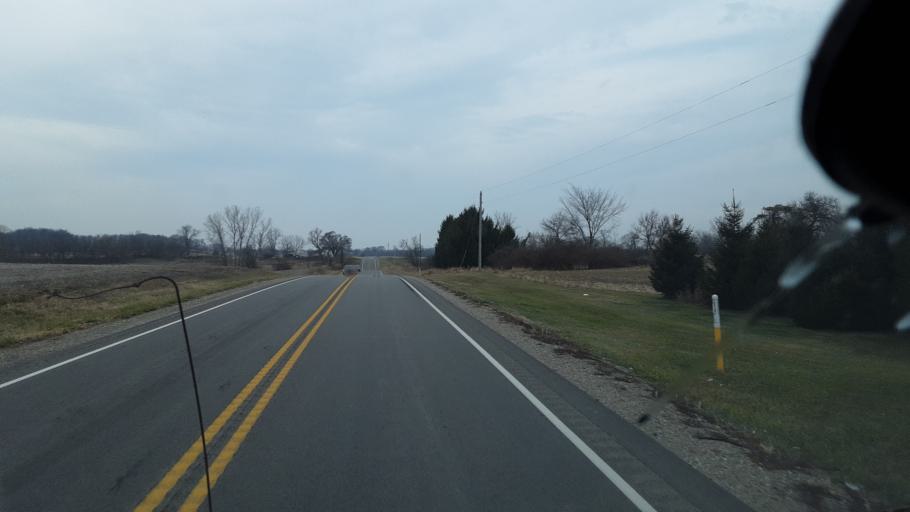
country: US
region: Indiana
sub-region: Steuben County
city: Angola
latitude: 41.5984
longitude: -85.1692
